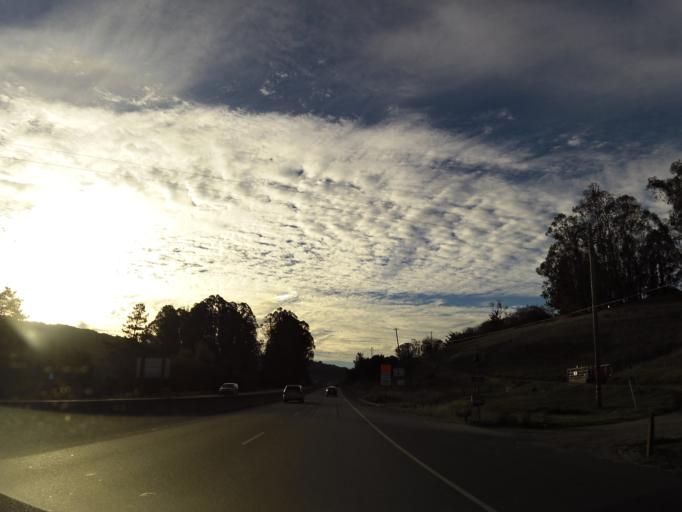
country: US
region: California
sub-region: San Benito County
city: Aromas
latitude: 36.8427
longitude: -121.6336
